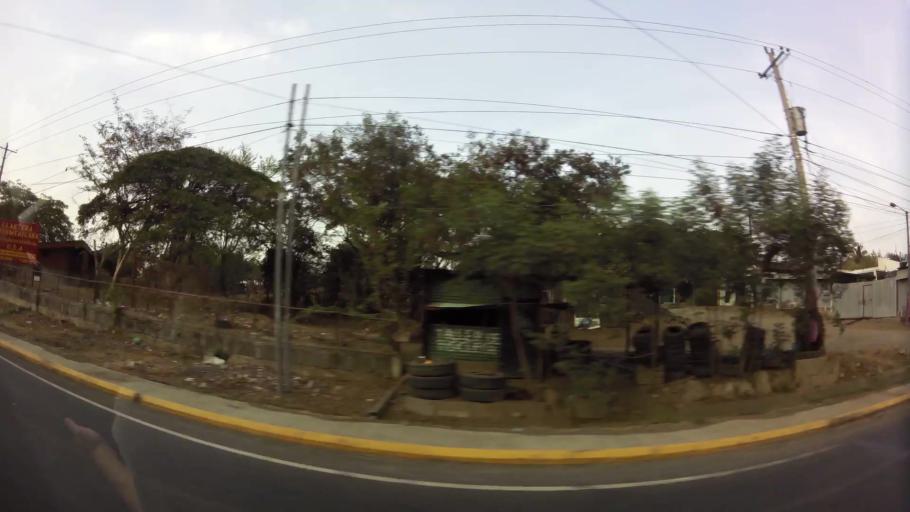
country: NI
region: Managua
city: Ciudad Sandino
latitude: 12.1417
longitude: -86.3344
